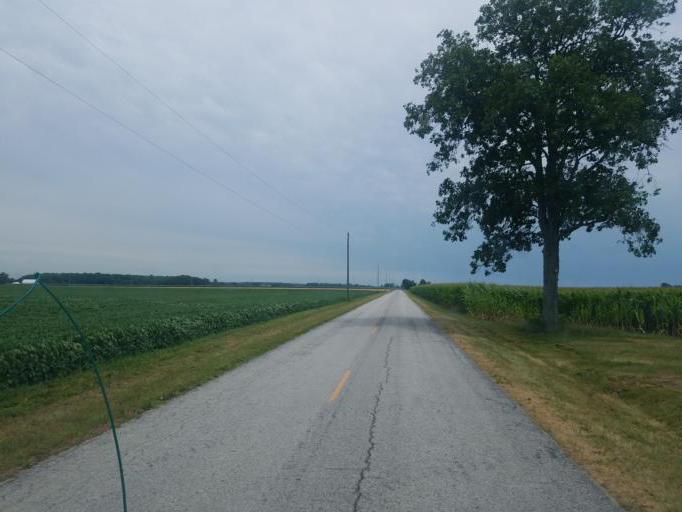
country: US
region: Ohio
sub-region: Defiance County
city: Hicksville
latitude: 41.2372
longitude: -84.7644
